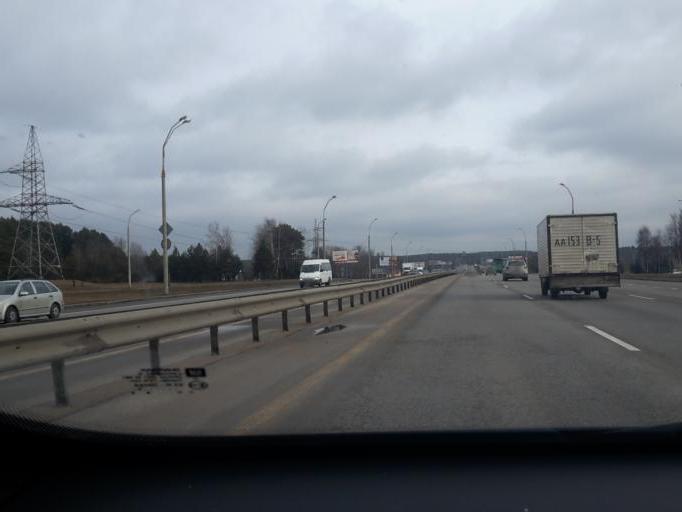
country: BY
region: Minsk
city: Zhdanovichy
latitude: 53.9512
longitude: 27.4464
